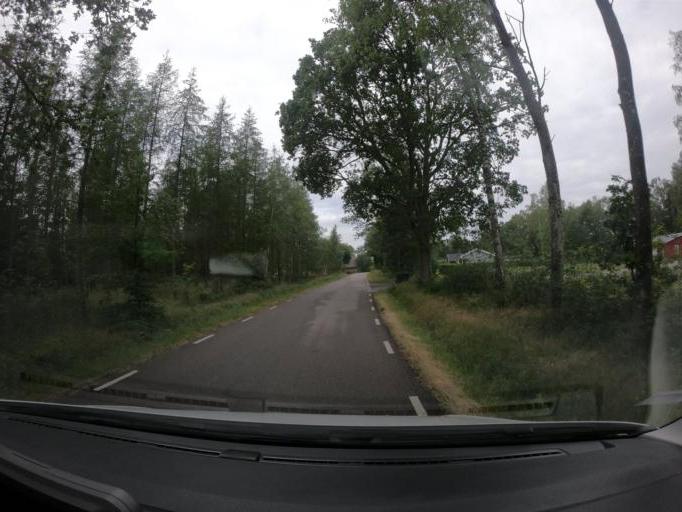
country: SE
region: Skane
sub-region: Klippans Kommun
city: Klippan
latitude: 56.2666
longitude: 13.1461
